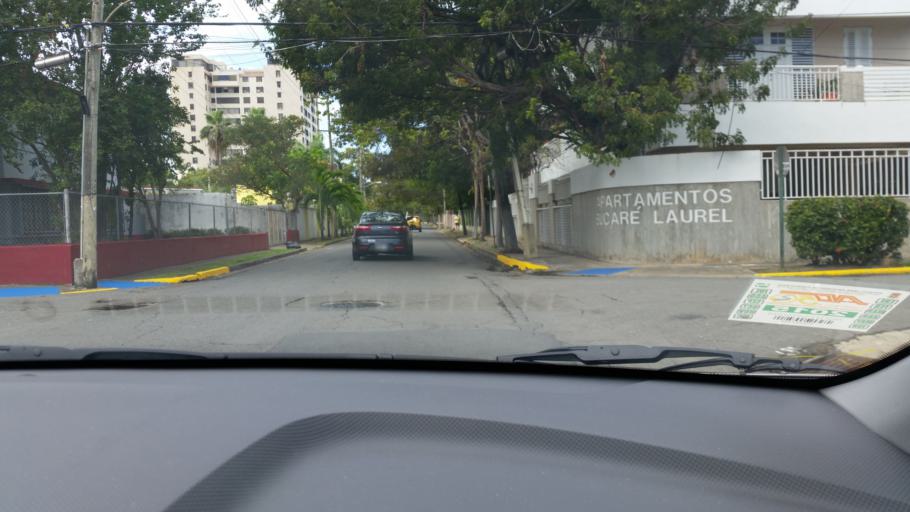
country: PR
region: San Juan
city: San Juan
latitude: 18.4518
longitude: -66.0412
